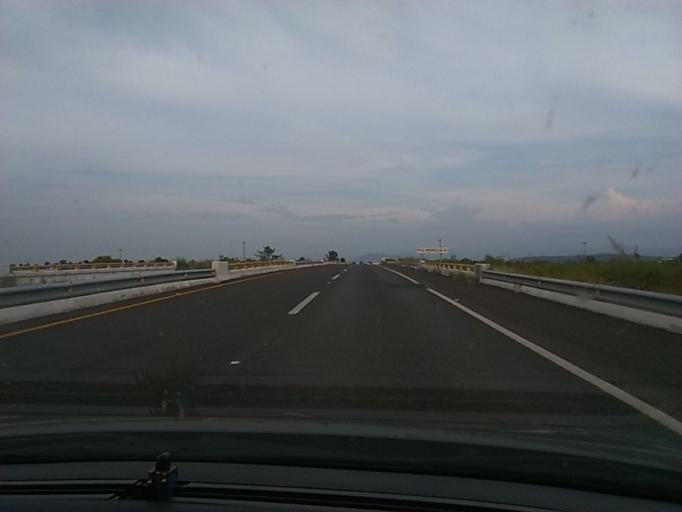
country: MX
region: Michoacan
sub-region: Alvaro Obregon
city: Lazaro Cardenas (La Purisima)
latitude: 19.8915
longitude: -101.0068
